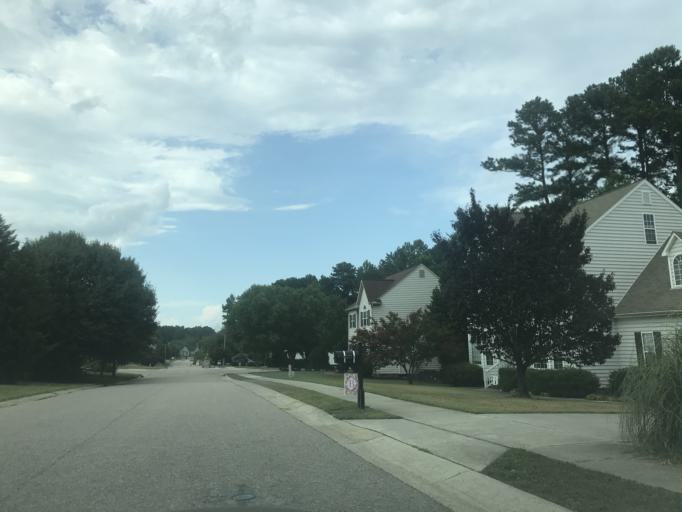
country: US
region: North Carolina
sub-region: Wake County
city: Knightdale
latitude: 35.8377
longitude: -78.5568
